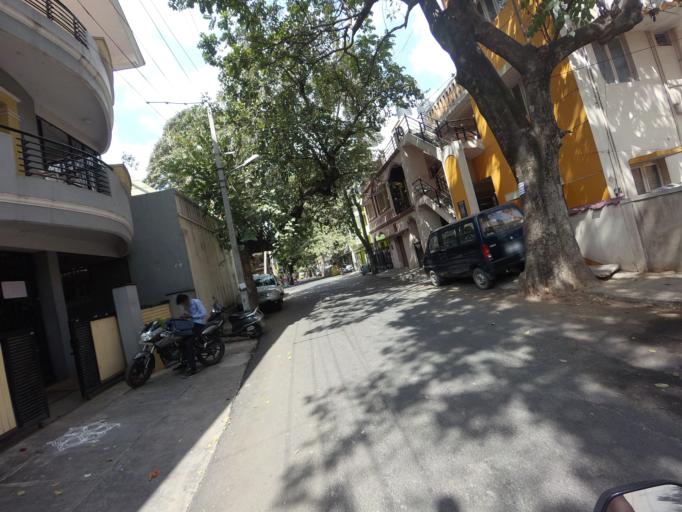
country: IN
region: Karnataka
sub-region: Bangalore Urban
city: Bangalore
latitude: 12.9569
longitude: 77.5357
